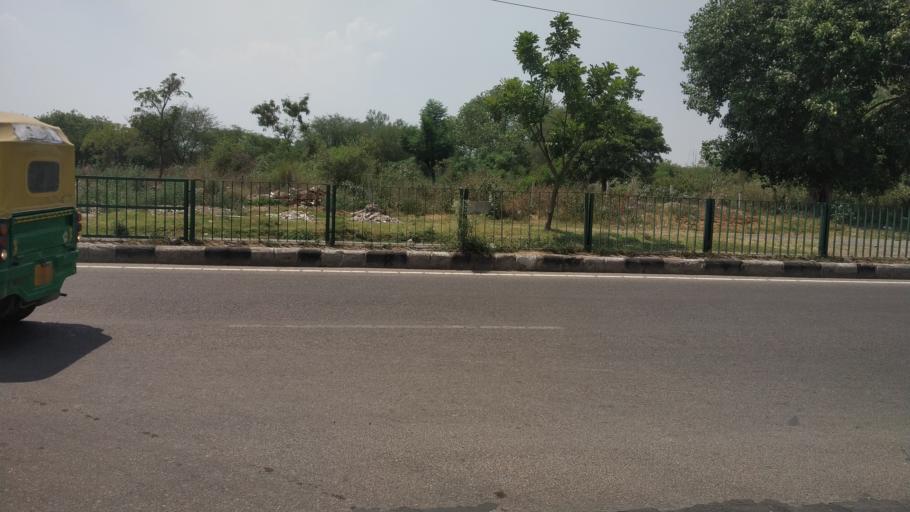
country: IN
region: Punjab
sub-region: Ajitgarh
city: Mohali
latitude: 30.7142
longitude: 76.7323
